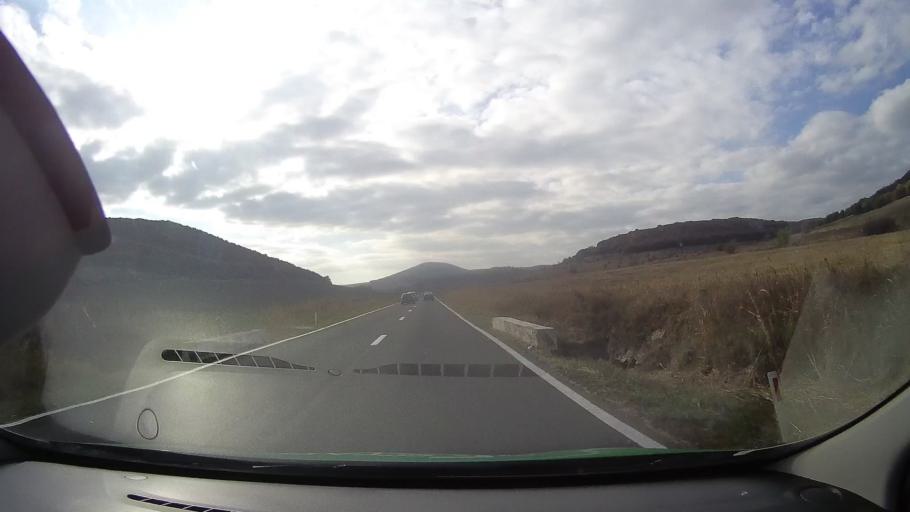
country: RO
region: Tulcea
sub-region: Comuna Ciucurova
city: Ciucurova
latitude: 44.9658
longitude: 28.5300
